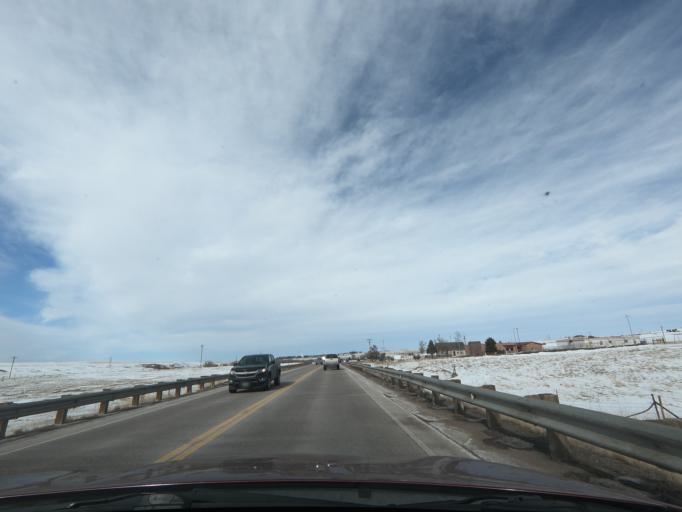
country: US
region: Colorado
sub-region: Elbert County
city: Elizabeth
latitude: 39.2265
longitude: -104.6999
